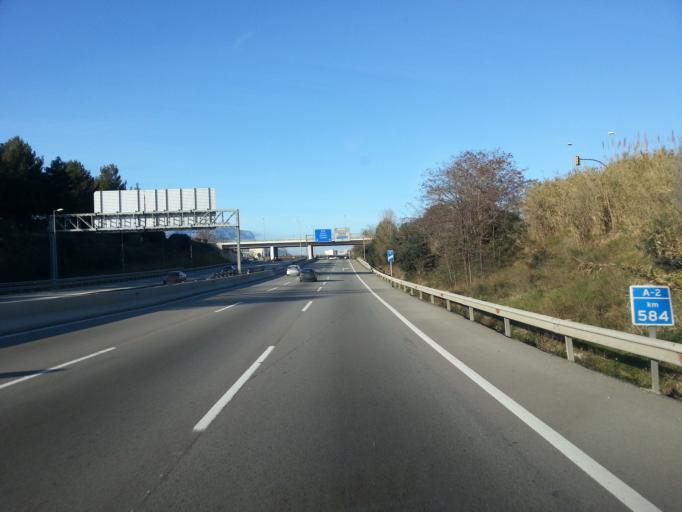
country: ES
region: Catalonia
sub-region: Provincia de Barcelona
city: Abrera
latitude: 41.5128
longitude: 1.8999
